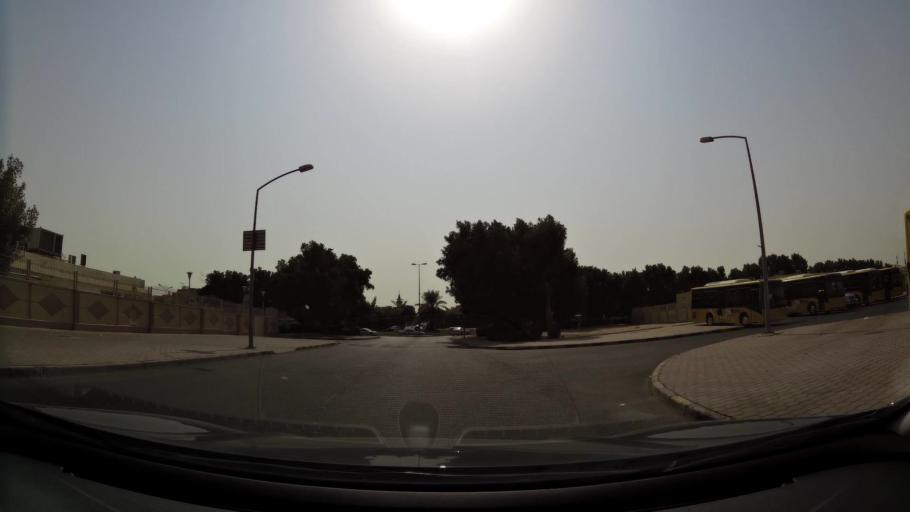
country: KW
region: Muhafazat al Jahra'
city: Al Jahra'
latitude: 29.3298
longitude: 47.6603
